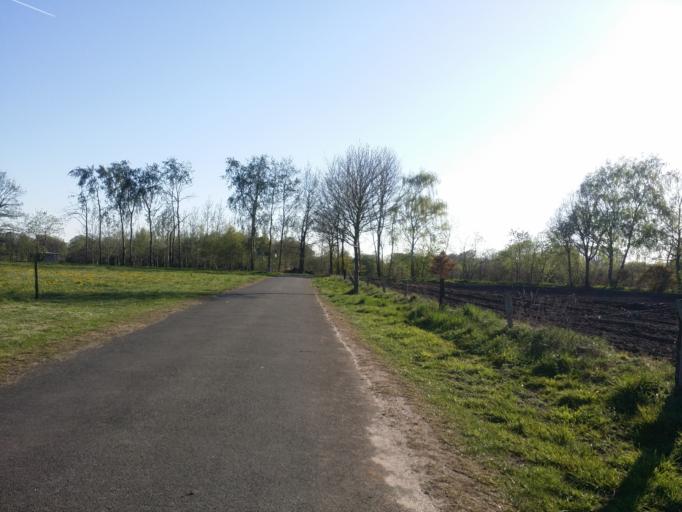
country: DE
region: Lower Saxony
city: Delmenhorst
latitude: 53.0122
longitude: 8.6545
